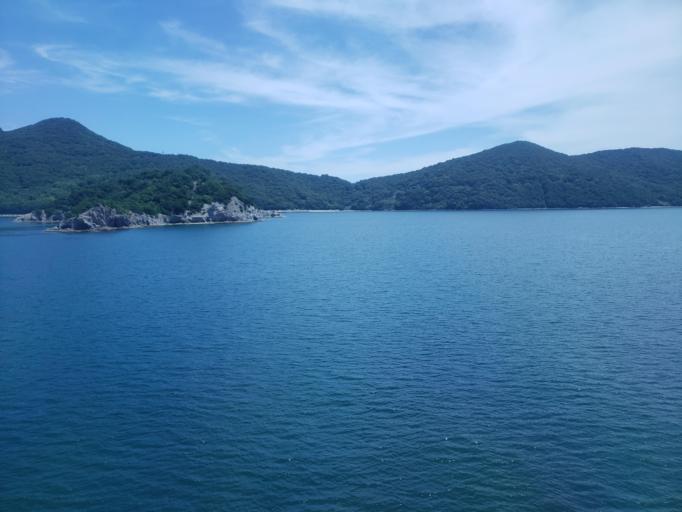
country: JP
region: Kagawa
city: Tonosho
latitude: 34.4439
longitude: 134.3165
